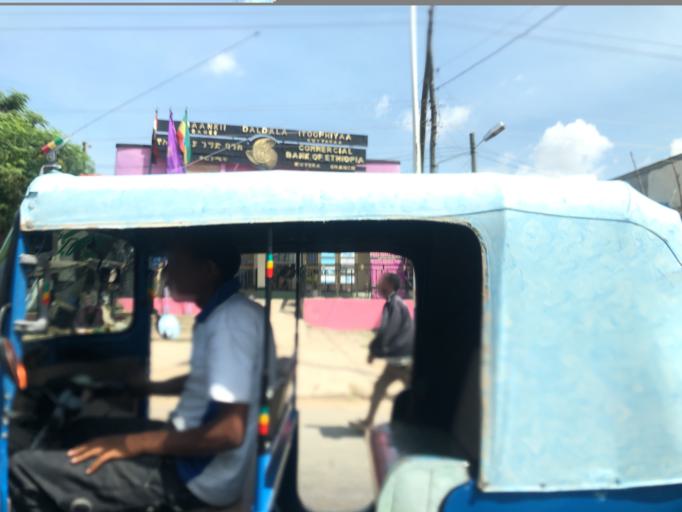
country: ET
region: Oromiya
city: Shashemene
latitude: 7.2655
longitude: 38.6573
